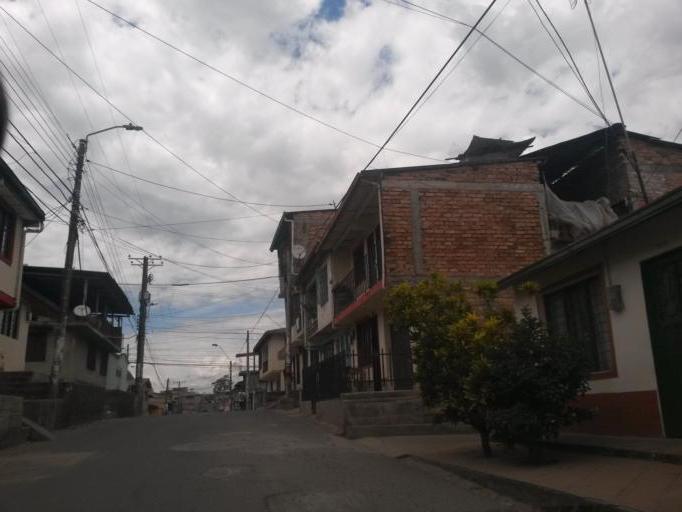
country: CO
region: Cauca
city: Popayan
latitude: 2.4479
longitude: -76.6271
